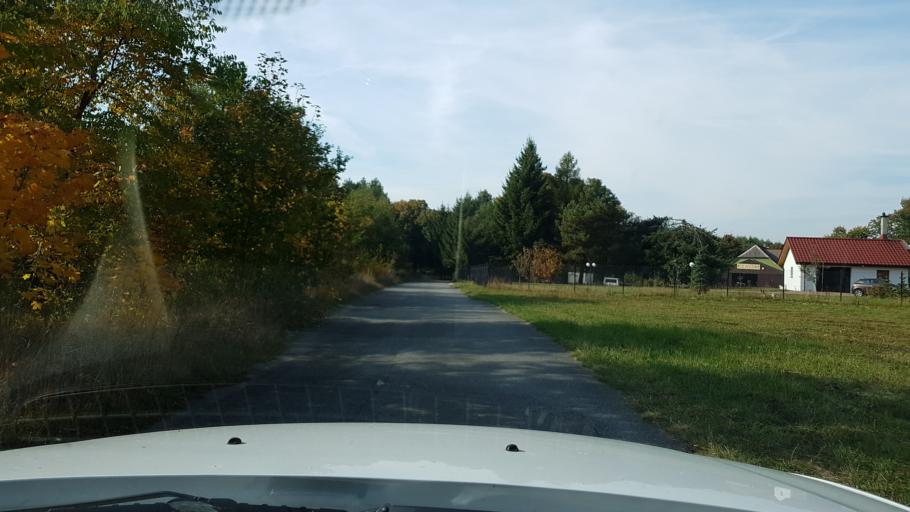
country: PL
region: West Pomeranian Voivodeship
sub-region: Powiat pyrzycki
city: Lipiany
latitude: 52.9335
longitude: 14.9524
